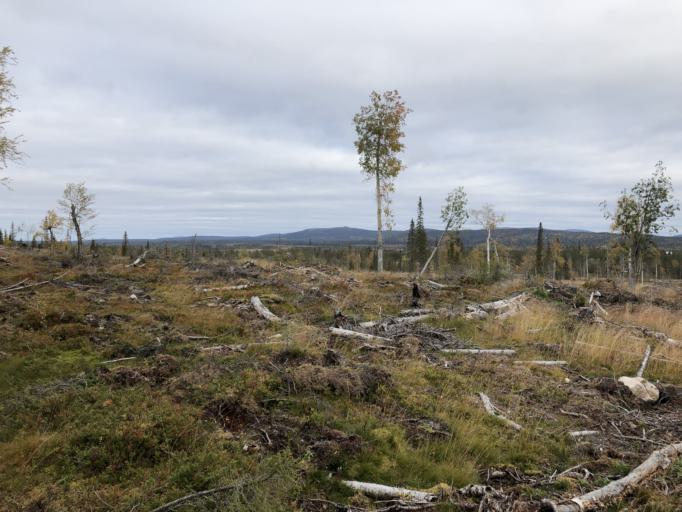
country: FI
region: Northern Ostrobothnia
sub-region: Koillismaa
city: Kuusamo
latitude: 66.5882
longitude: 29.3508
